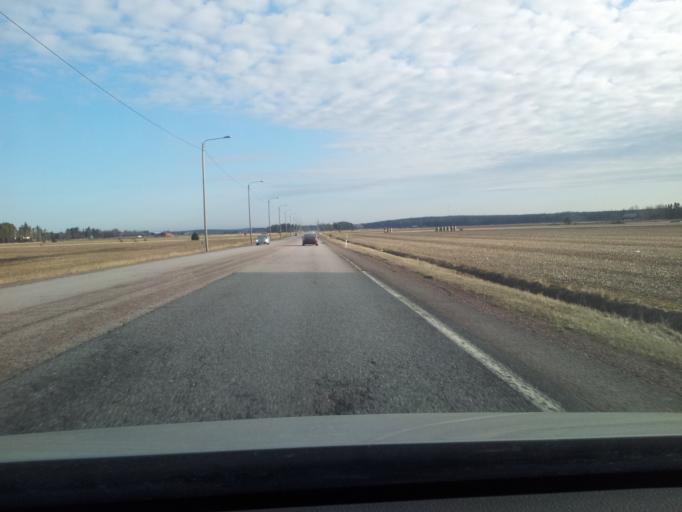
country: FI
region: Uusimaa
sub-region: Loviisa
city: Lapinjaervi
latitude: 60.6493
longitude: 26.2362
